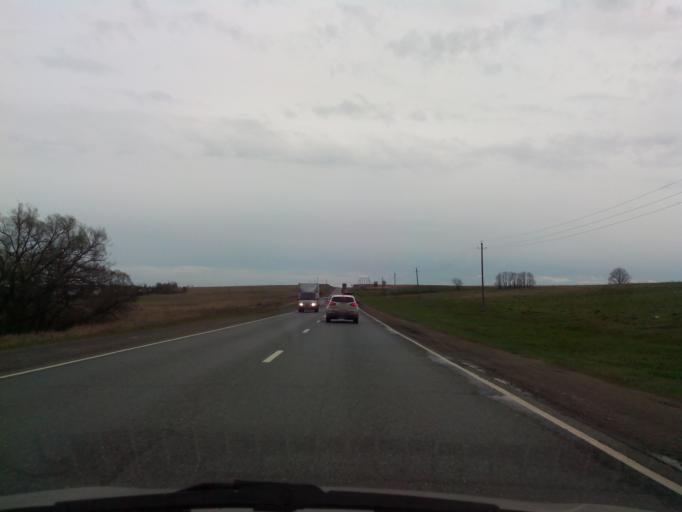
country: RU
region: Moskovskaya
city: Ozherel'ye
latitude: 54.7191
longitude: 38.2798
